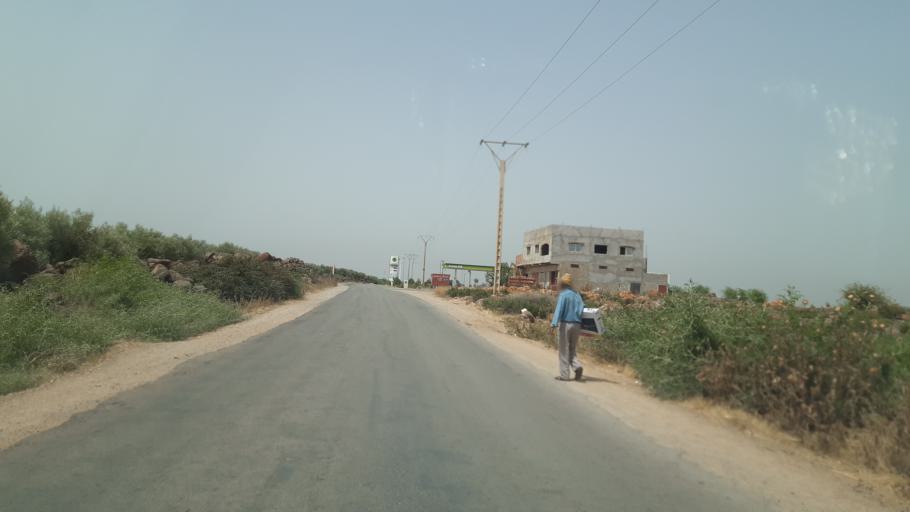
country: MA
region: Fes-Boulemane
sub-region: Fes
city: Oulad Tayeb
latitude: 33.8400
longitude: -5.1300
